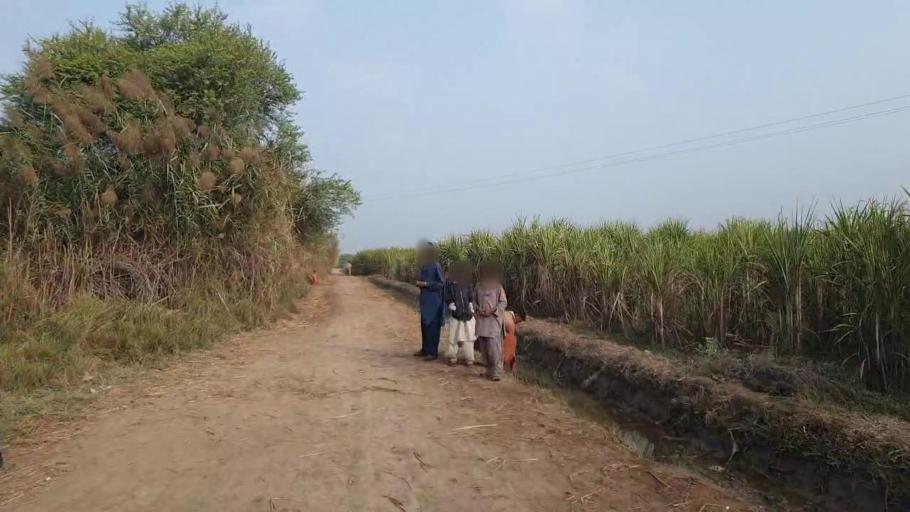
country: PK
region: Sindh
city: Tando Muhammad Khan
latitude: 25.1448
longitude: 68.5903
